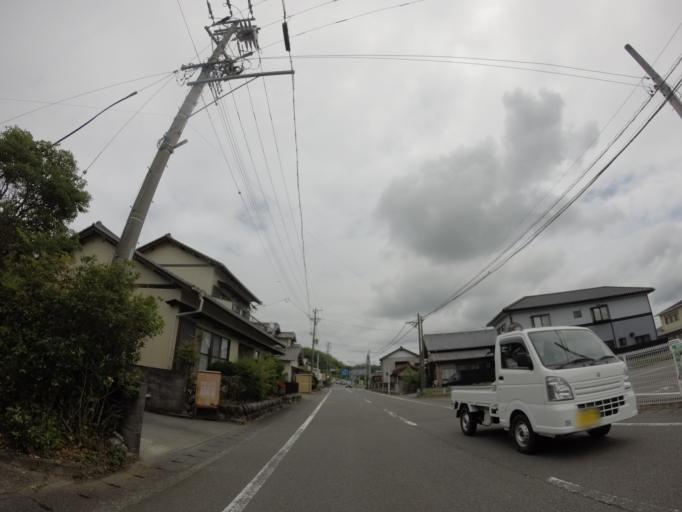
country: JP
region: Shizuoka
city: Shimada
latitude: 34.7672
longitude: 138.1883
